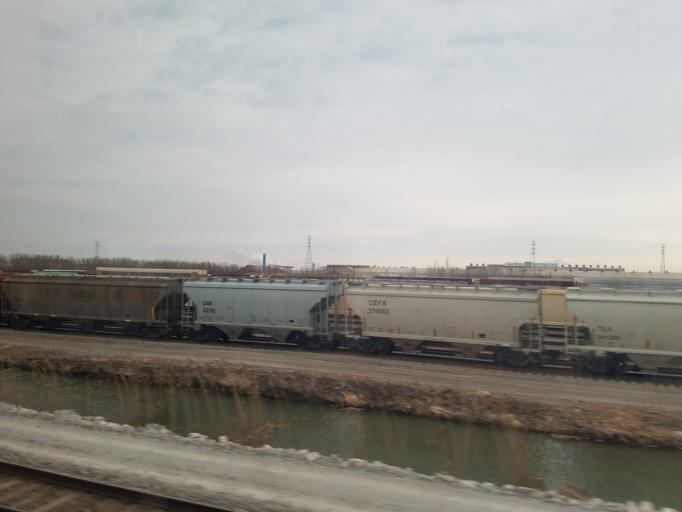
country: US
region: Indiana
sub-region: Lake County
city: Gary
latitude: 41.6150
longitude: -87.3661
